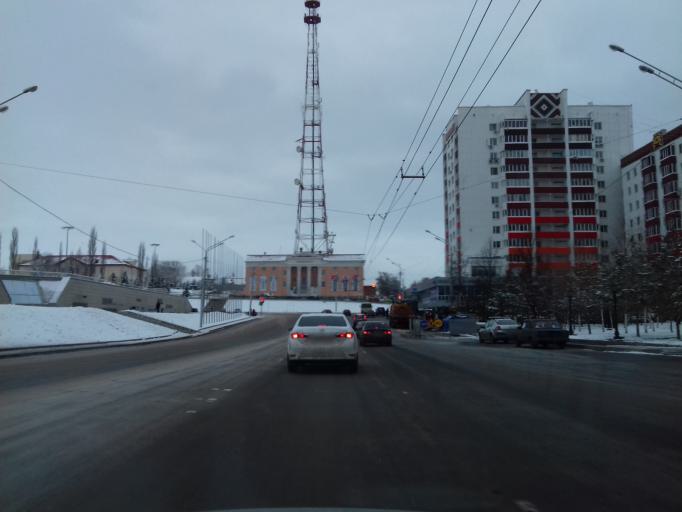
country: RU
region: Bashkortostan
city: Ufa
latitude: 54.7217
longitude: 55.9295
